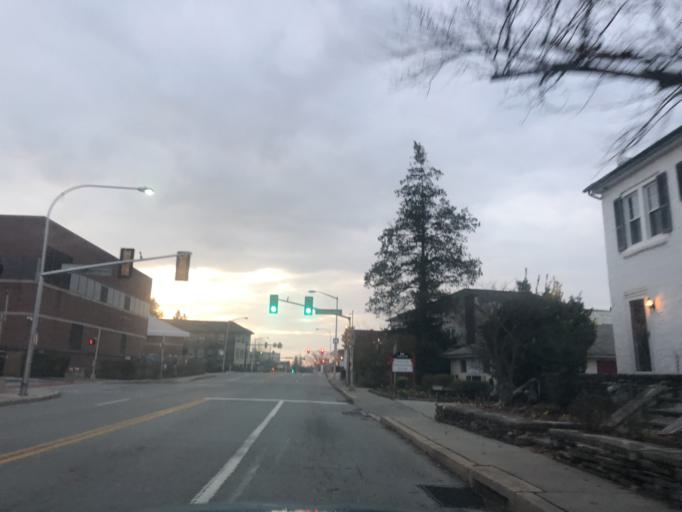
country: US
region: Pennsylvania
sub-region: Montgomery County
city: Bryn Mawr
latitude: 40.0191
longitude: -75.3231
